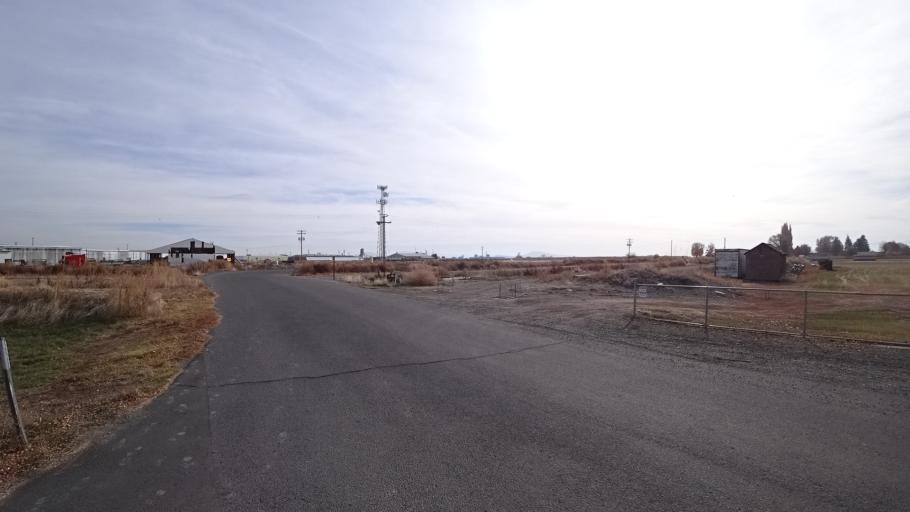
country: US
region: California
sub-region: Siskiyou County
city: Tulelake
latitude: 41.9510
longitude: -121.4723
